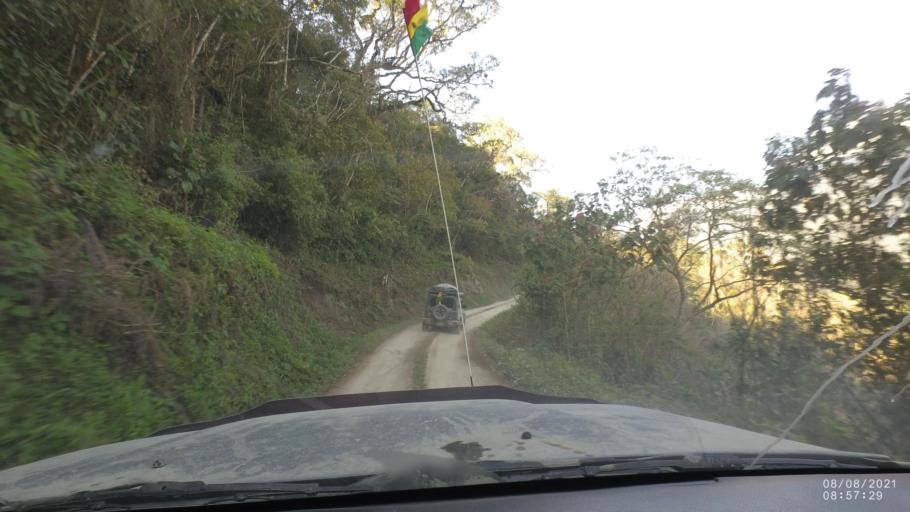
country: BO
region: La Paz
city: Quime
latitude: -16.5486
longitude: -66.7448
